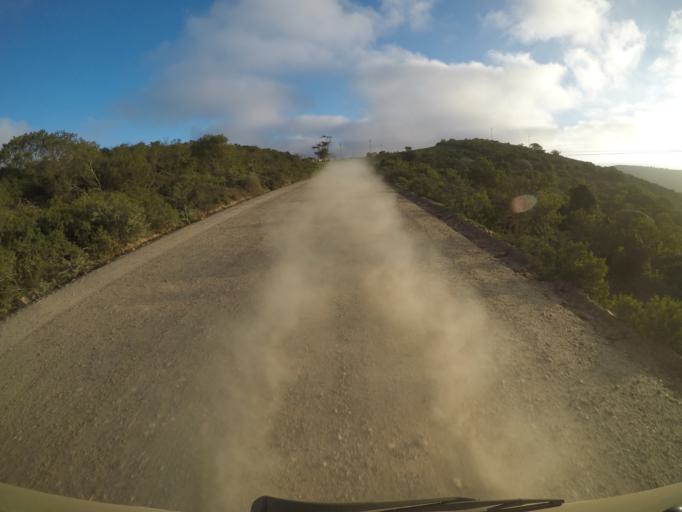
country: ZA
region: Western Cape
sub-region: Eden District Municipality
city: Mossel Bay
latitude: -34.1294
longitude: 22.0478
